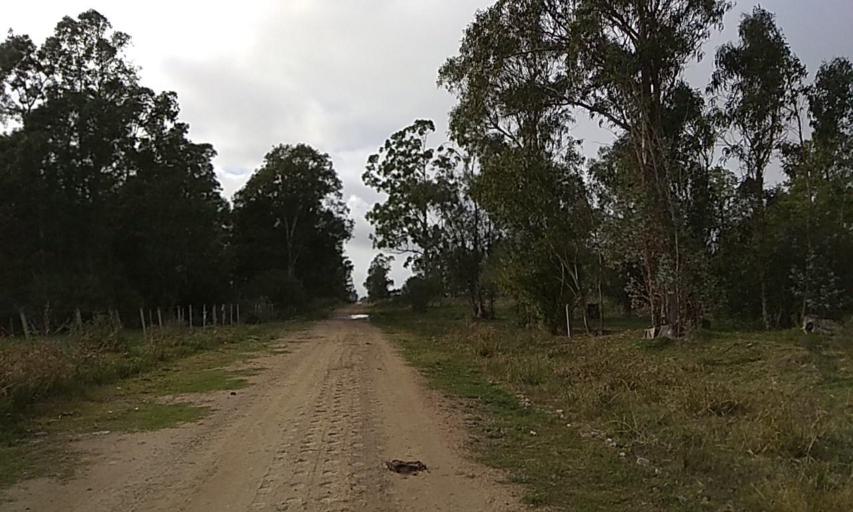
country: UY
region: Florida
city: Florida
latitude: -34.0754
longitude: -56.2314
